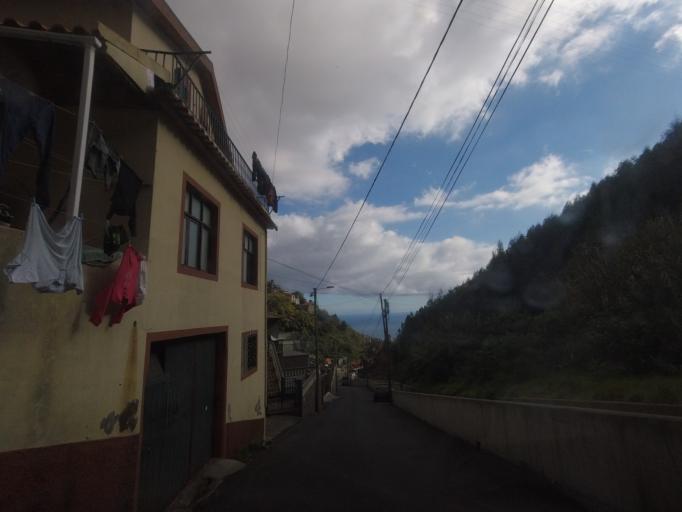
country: PT
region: Madeira
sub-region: Funchal
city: Nossa Senhora do Monte
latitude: 32.6761
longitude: -16.9314
